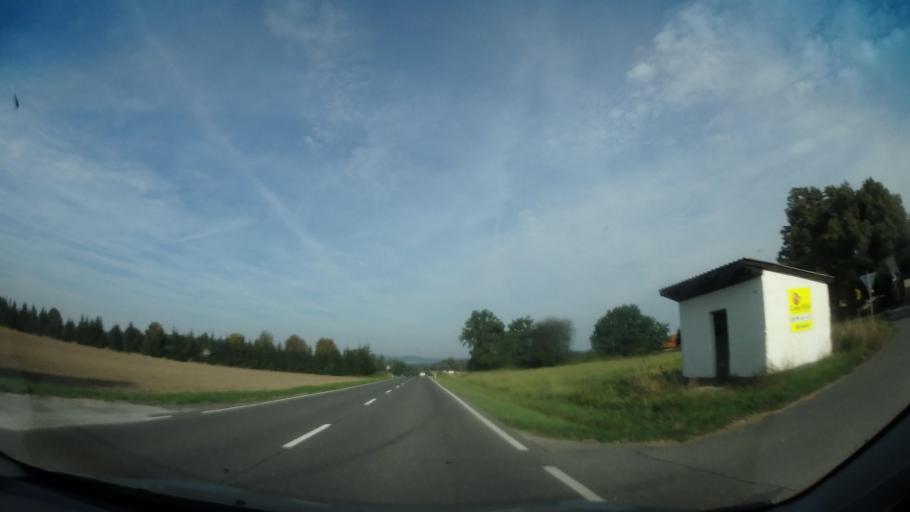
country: CZ
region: Jihocesky
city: Cimelice
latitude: 49.4367
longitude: 14.1427
